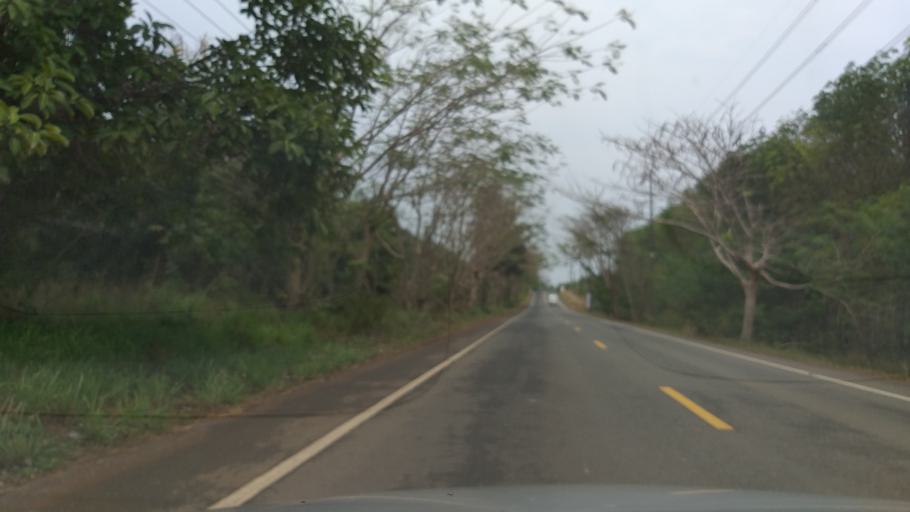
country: TH
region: Trat
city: Laem Ngop
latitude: 12.2623
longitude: 102.2962
